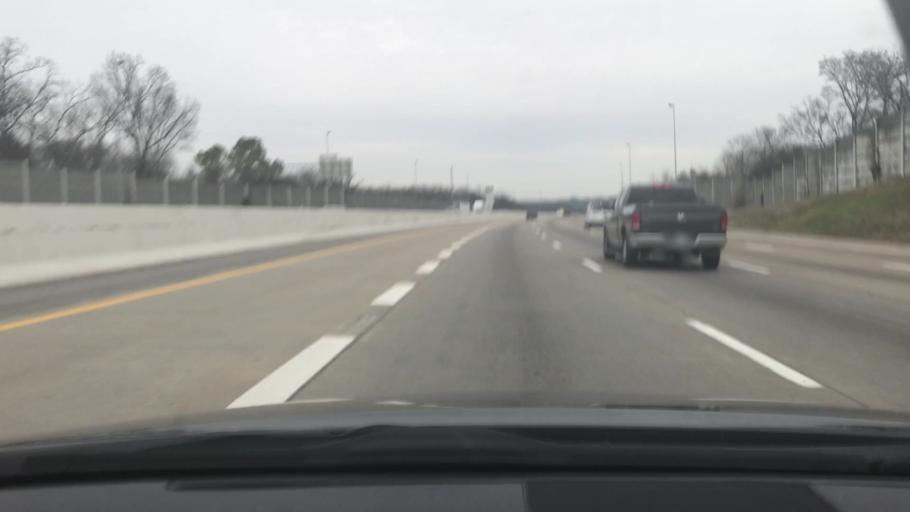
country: US
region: Tennessee
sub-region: Davidson County
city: Goodlettsville
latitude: 36.2810
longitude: -86.7326
